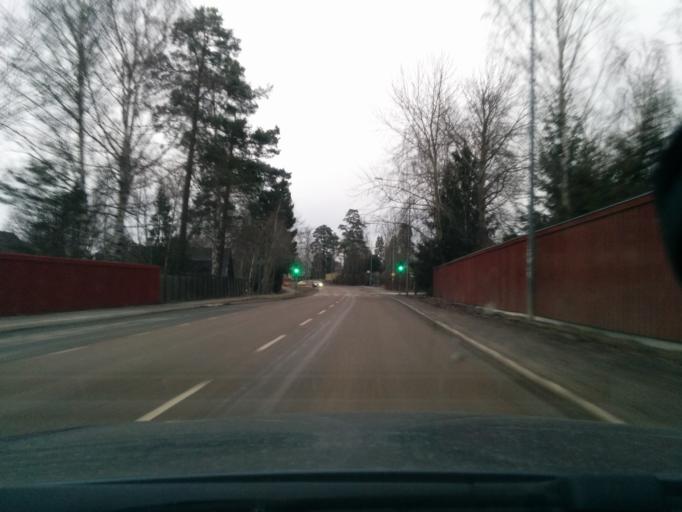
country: SE
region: Stockholm
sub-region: Taby Kommun
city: Taby
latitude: 59.4616
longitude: 18.0403
